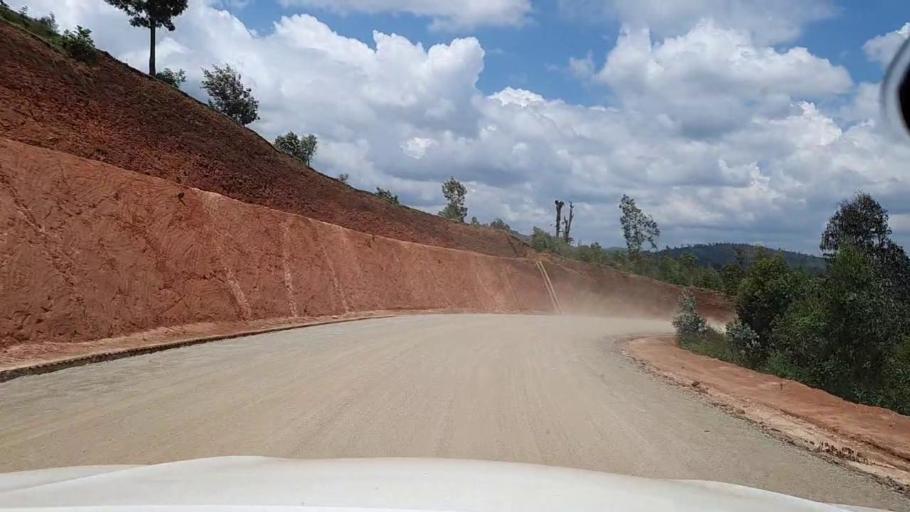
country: RW
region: Southern Province
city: Butare
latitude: -2.6955
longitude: 29.5594
